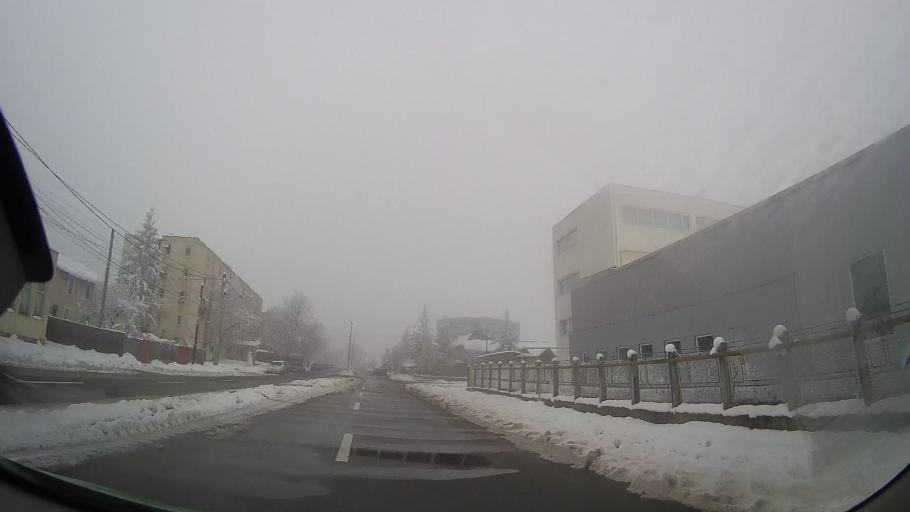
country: RO
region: Iasi
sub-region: Municipiul Pascani
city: Pascani
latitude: 47.2401
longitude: 26.7296
